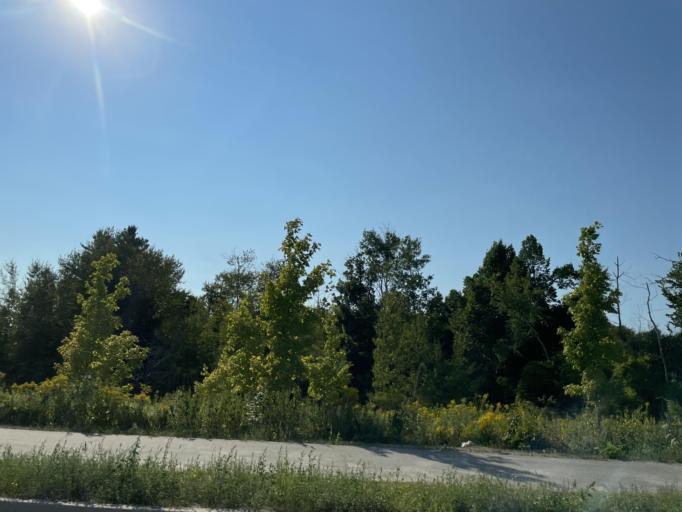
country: CA
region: Ontario
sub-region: Wellington County
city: Guelph
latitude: 43.4888
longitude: -80.2173
